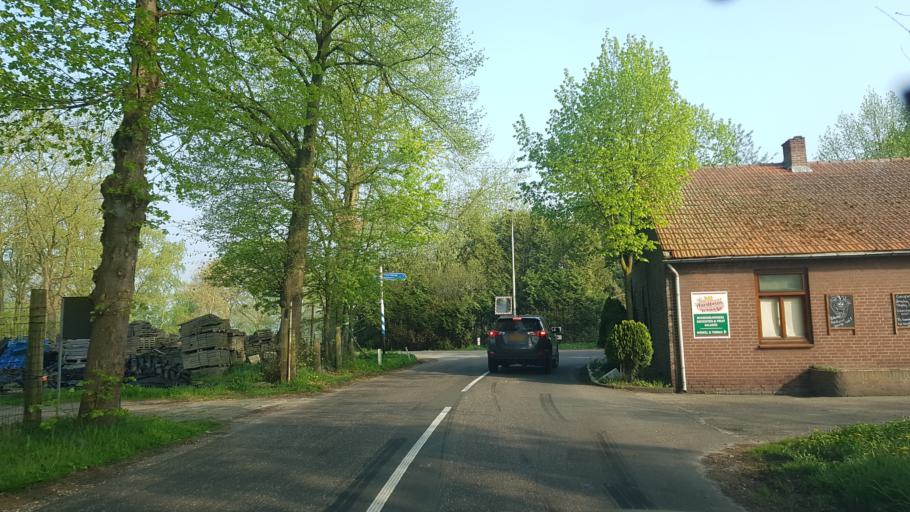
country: NL
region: Limburg
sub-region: Gemeente Nederweert
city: Nederweert
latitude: 51.3200
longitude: 5.7000
